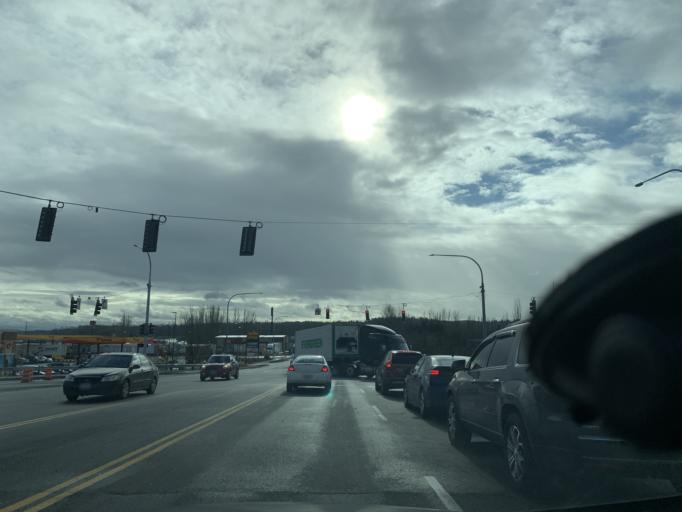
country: US
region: Washington
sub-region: Pierce County
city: Fife
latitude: 47.2464
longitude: -122.3857
